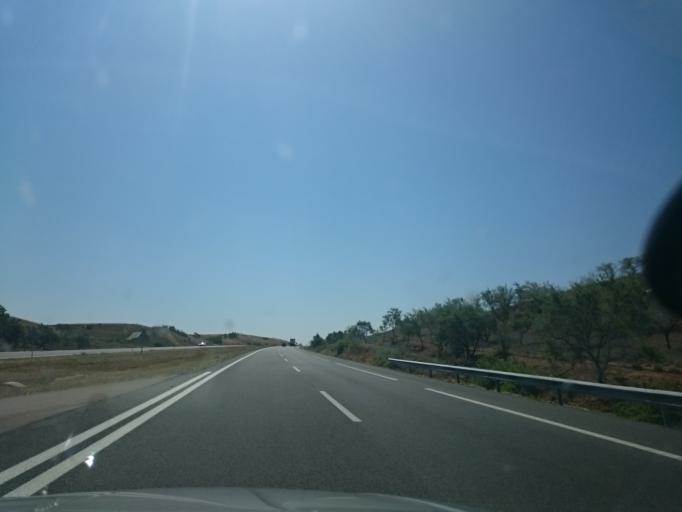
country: ES
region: Navarre
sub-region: Provincia de Navarra
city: Ribaforada
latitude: 41.9781
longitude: -1.5543
